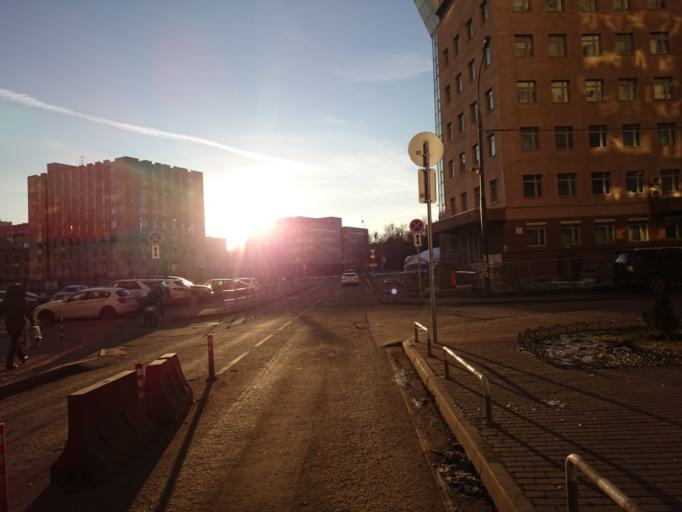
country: RU
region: Moscow
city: Sokol
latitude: 55.7853
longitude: 37.5220
